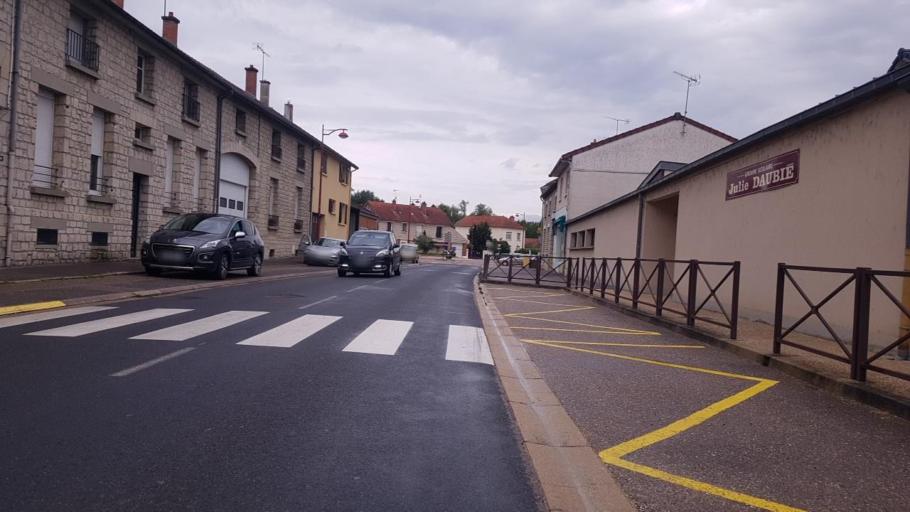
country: FR
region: Champagne-Ardenne
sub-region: Departement de la Marne
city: Vitry-le-Francois
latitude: 48.7444
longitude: 4.6282
